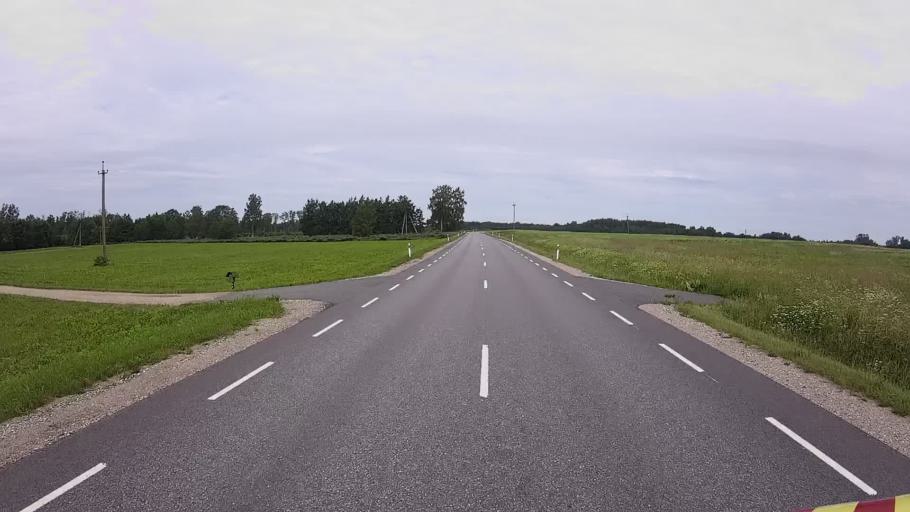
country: EE
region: Viljandimaa
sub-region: Karksi vald
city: Karksi-Nuia
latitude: 58.1644
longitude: 25.5849
